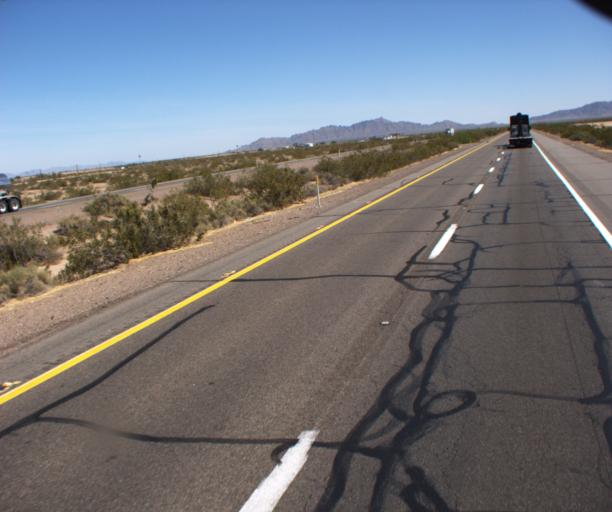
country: US
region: Arizona
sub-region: Yuma County
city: Wellton
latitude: 32.7003
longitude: -113.9077
